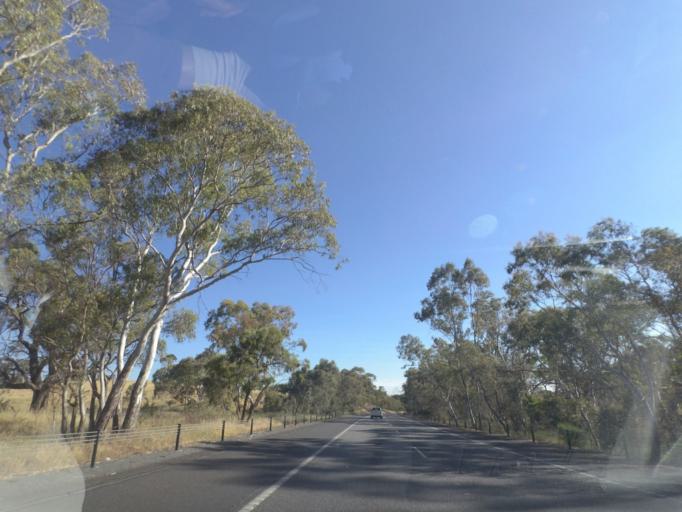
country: AU
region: Victoria
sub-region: Murrindindi
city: Kinglake West
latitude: -37.1675
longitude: 145.0776
